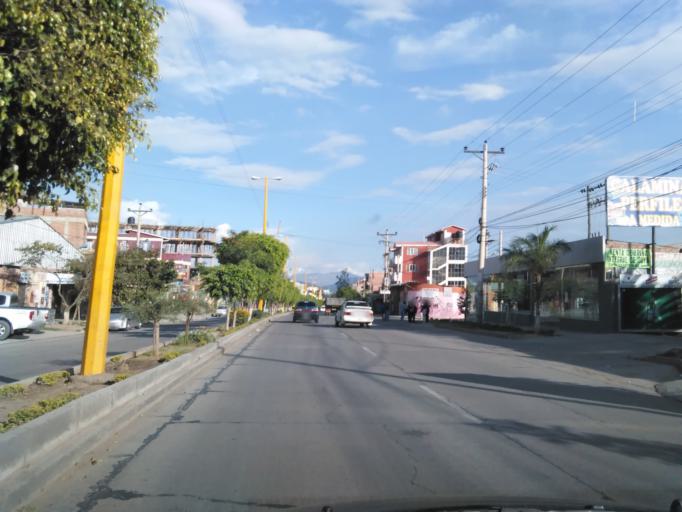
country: BO
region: Cochabamba
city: Cochabamba
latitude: -17.3512
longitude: -66.1921
